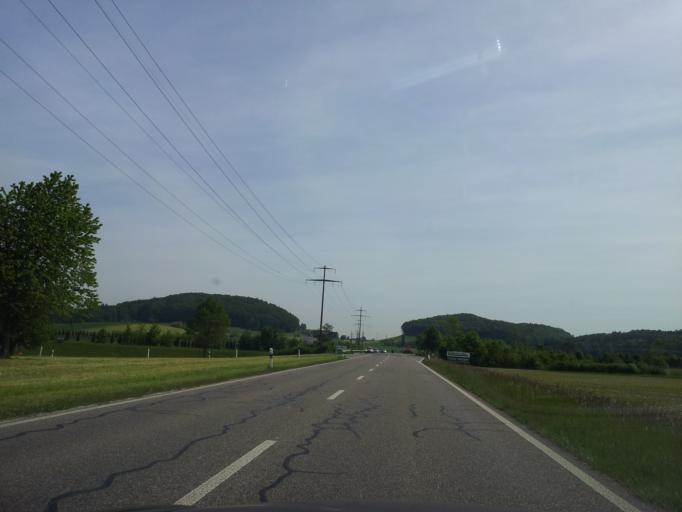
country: CH
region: Zurich
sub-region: Bezirk Buelach
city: Rafz
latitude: 47.6021
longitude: 8.5485
